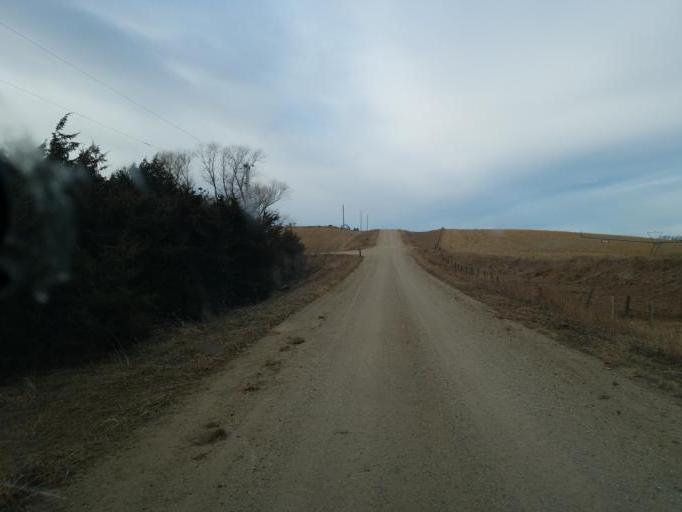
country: US
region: Nebraska
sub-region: Knox County
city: Bloomfield
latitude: 42.5576
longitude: -97.7439
